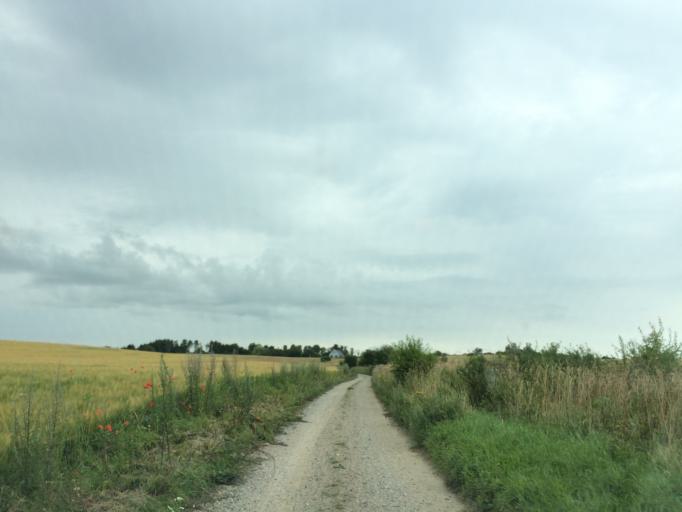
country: DK
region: Central Jutland
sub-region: Syddjurs Kommune
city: Ronde
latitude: 56.2362
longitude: 10.5505
